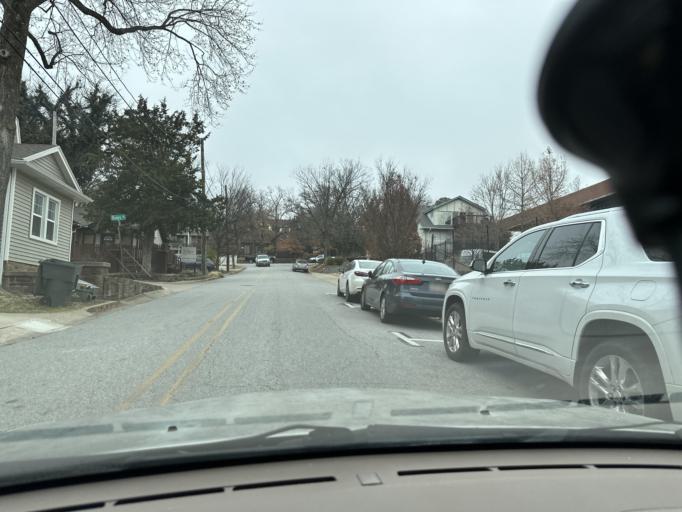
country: US
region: Arkansas
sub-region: Washington County
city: Fayetteville
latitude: 36.0677
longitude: -94.1608
